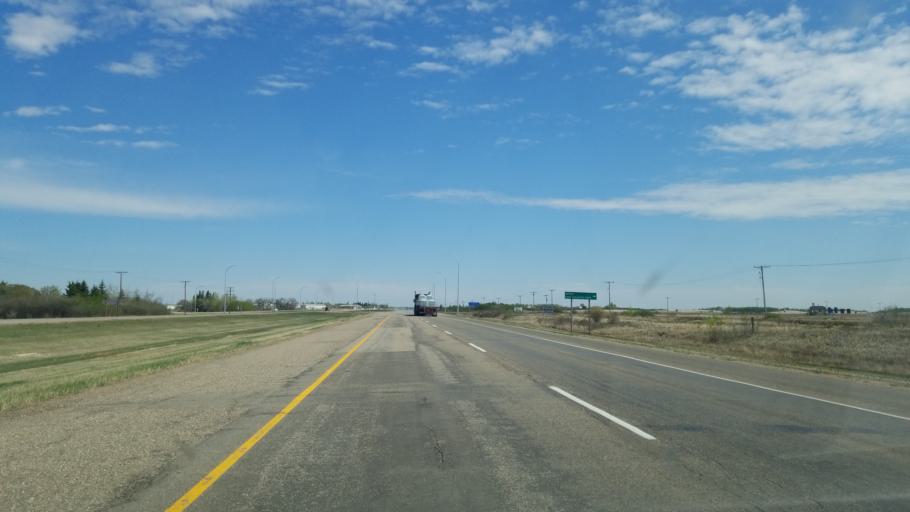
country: CA
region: Saskatchewan
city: Lloydminster
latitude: 53.1341
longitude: -109.6411
